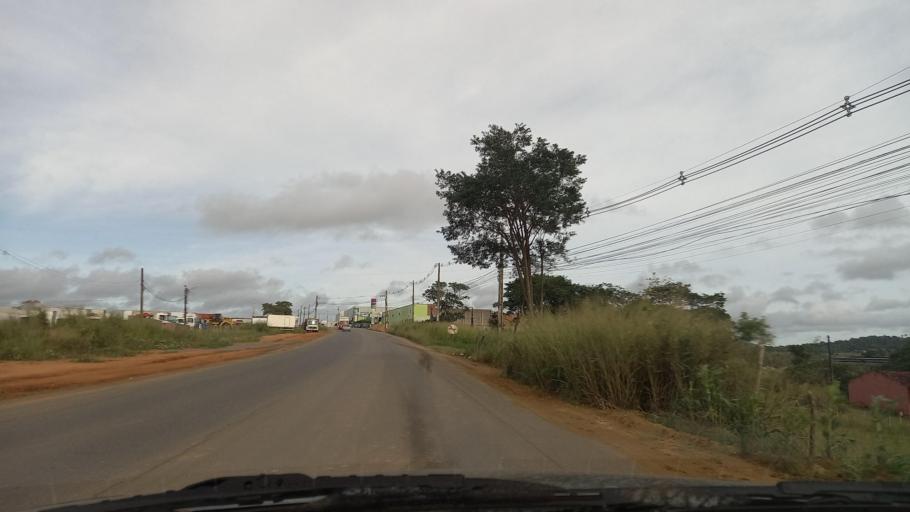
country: BR
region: Pernambuco
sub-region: Vitoria De Santo Antao
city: Vitoria de Santo Antao
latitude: -8.1214
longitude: -35.3296
